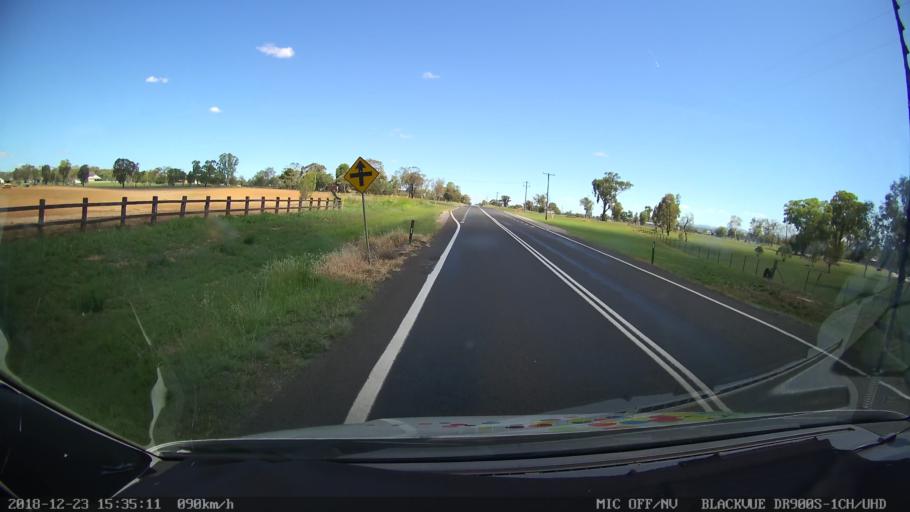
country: AU
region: New South Wales
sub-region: Tamworth Municipality
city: Tamworth
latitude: -31.0238
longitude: 150.8814
